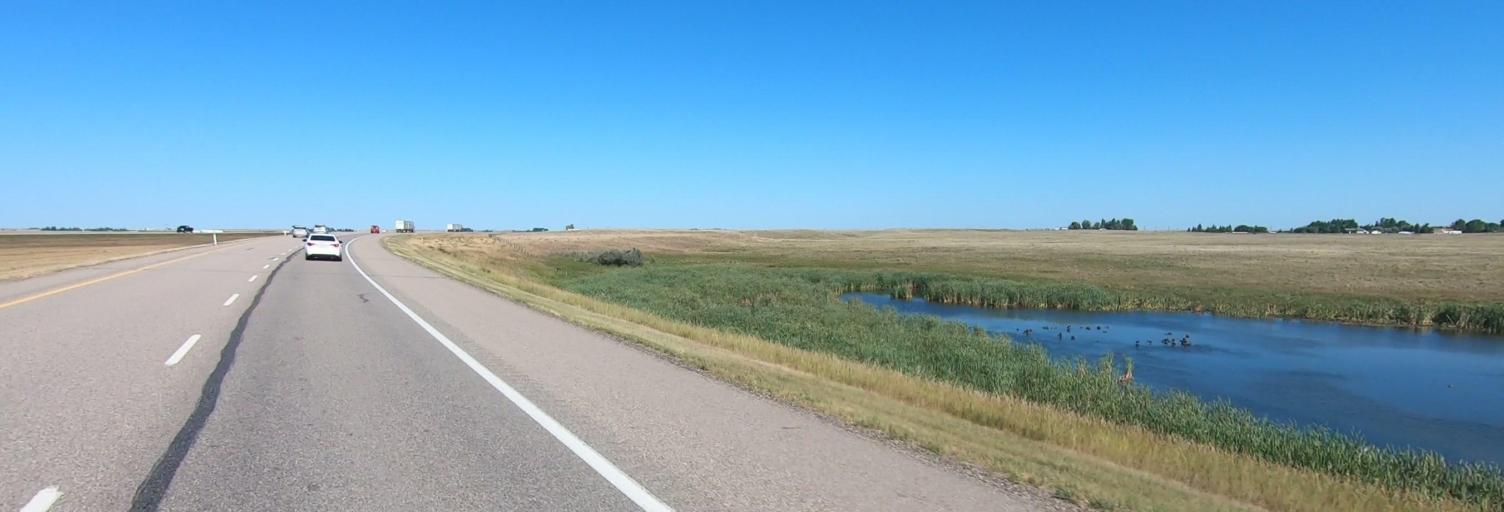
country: CA
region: Alberta
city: Bassano
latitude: 50.7654
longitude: -112.4005
